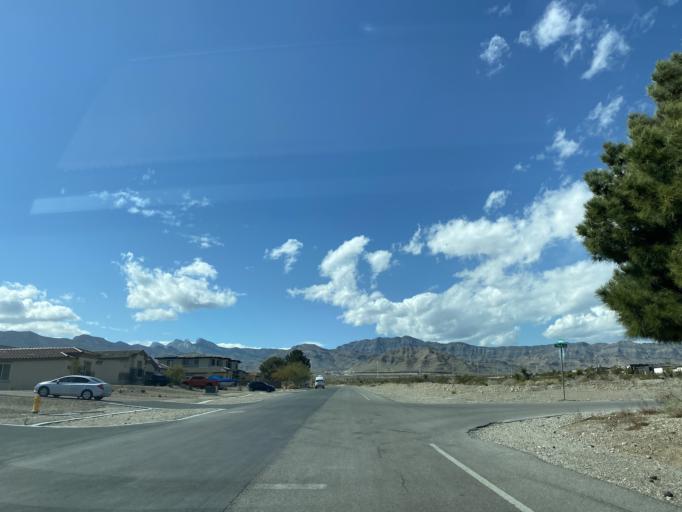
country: US
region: Nevada
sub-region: Clark County
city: Summerlin South
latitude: 36.2555
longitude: -115.3037
